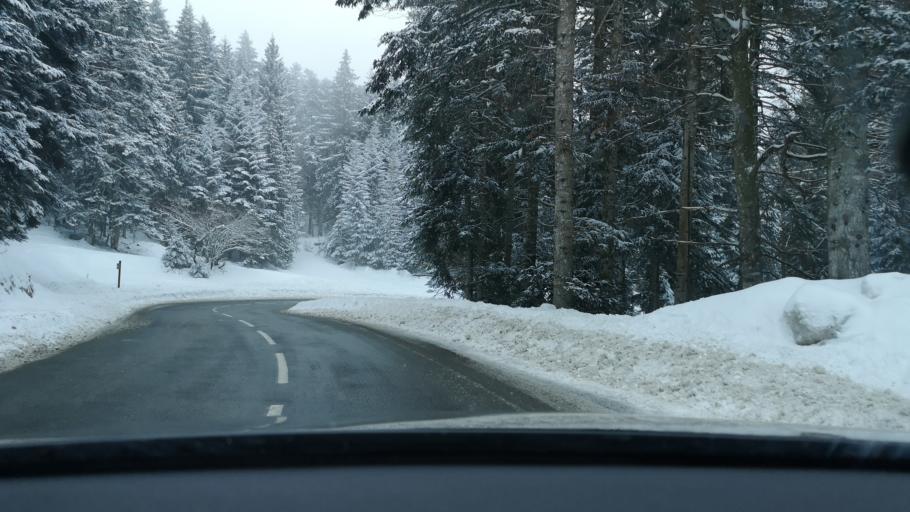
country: FR
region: Rhone-Alpes
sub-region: Departement de l'Ain
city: Oyonnax
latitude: 46.2287
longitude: 5.7083
